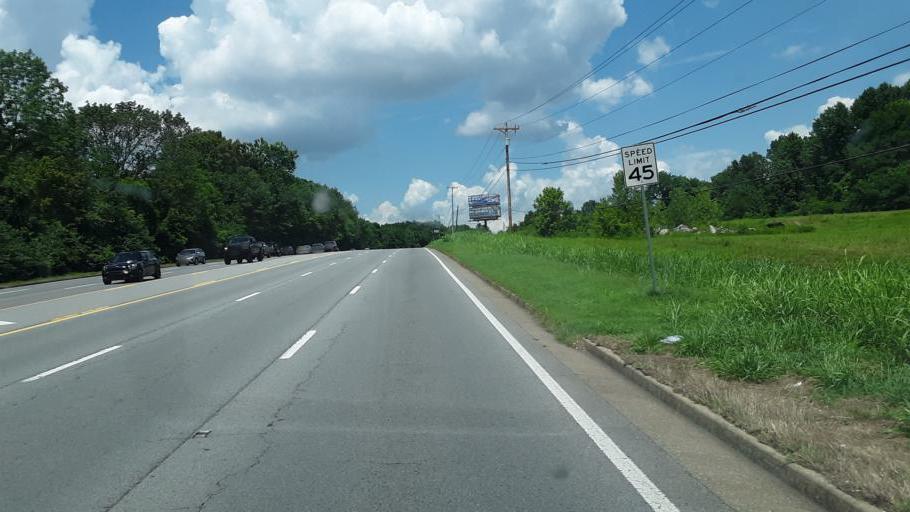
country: US
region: Kentucky
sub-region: Christian County
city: Fort Campbell North
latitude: 36.6087
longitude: -87.4275
